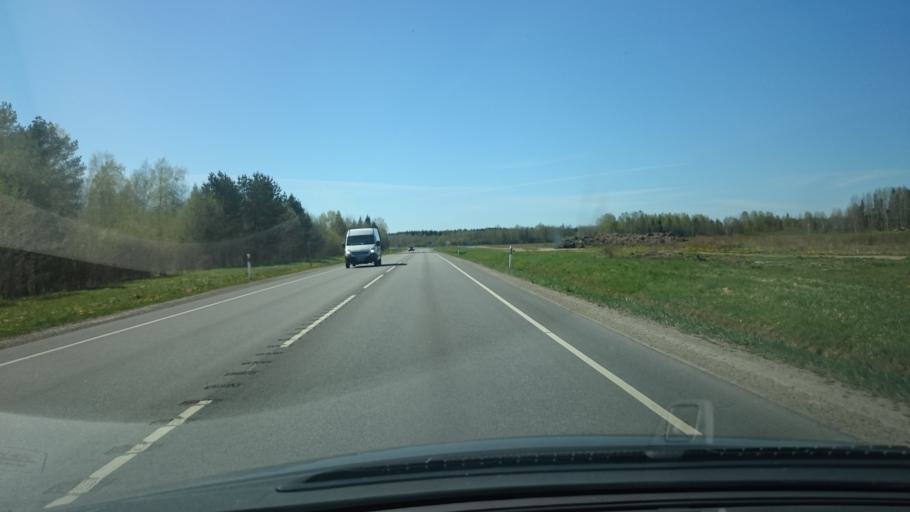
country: EE
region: Ida-Virumaa
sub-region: Johvi vald
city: Johvi
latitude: 59.3669
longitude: 27.4284
